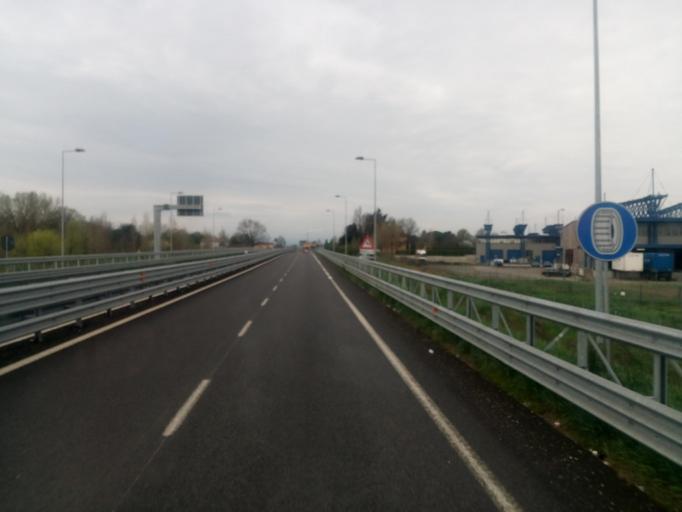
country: IT
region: Emilia-Romagna
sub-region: Forli-Cesena
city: Forli
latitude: 44.2462
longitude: 12.0945
